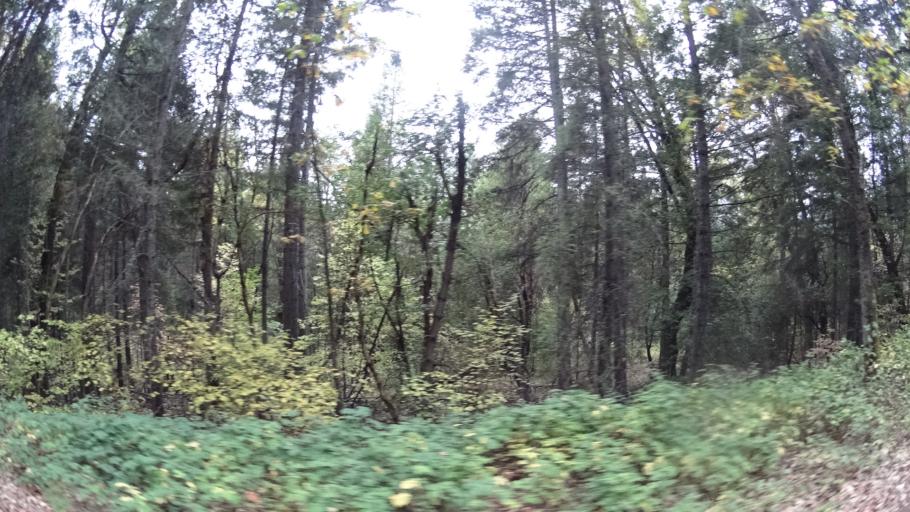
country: US
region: California
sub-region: Siskiyou County
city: Happy Camp
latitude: 41.8094
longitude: -123.3367
